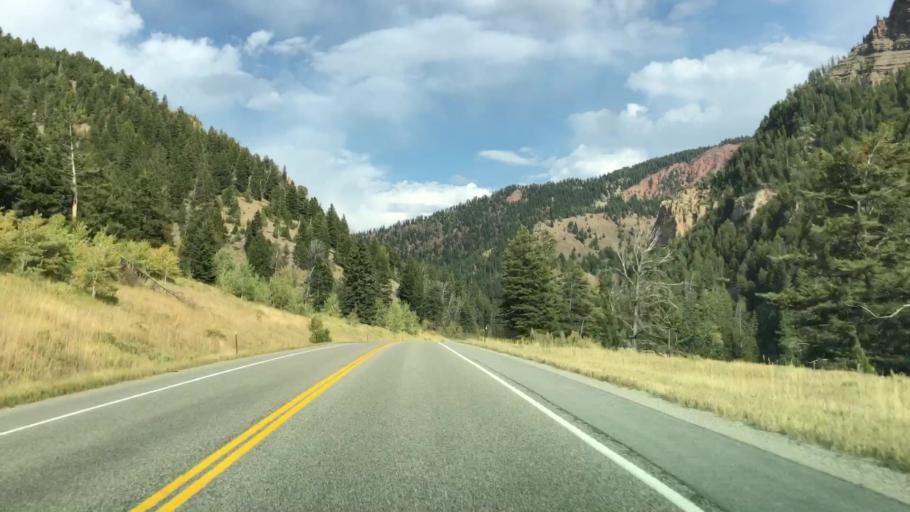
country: US
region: Wyoming
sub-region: Teton County
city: Hoback
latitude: 43.2818
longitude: -110.5900
